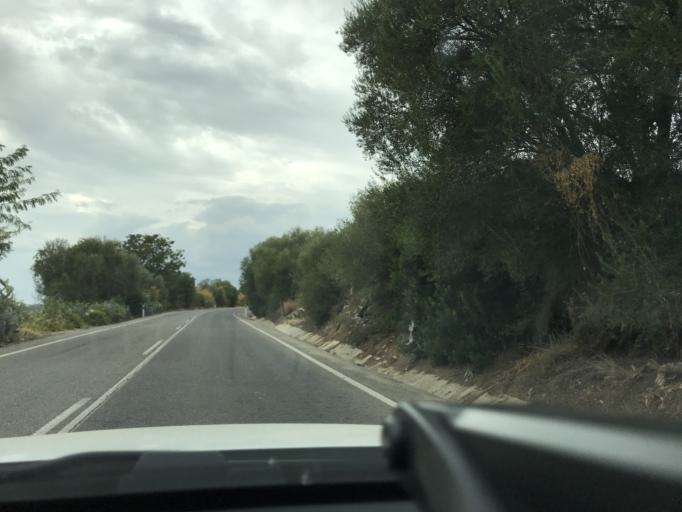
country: ES
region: Andalusia
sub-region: Provincia de Sevilla
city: Villanueva del Rio y Minas
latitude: 37.6348
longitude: -5.7254
